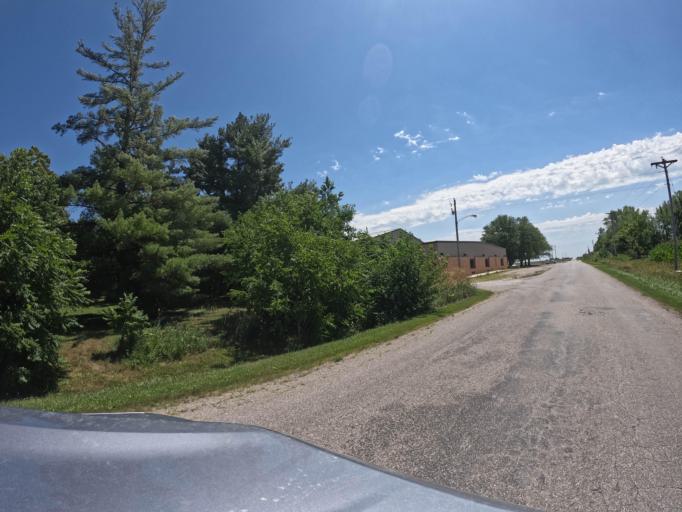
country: US
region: Iowa
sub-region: Keokuk County
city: Sigourney
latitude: 41.4537
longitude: -92.3357
